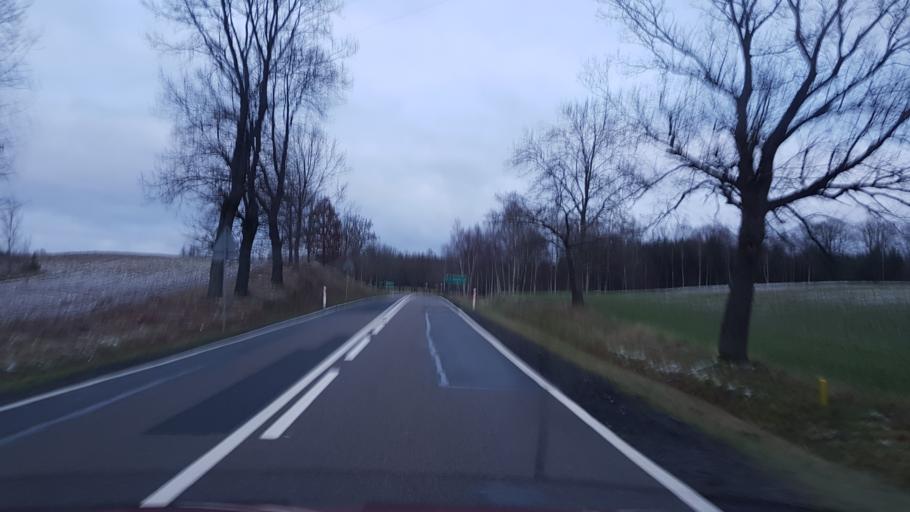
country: PL
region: Pomeranian Voivodeship
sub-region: Powiat bytowski
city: Tuchomie
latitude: 54.0712
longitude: 17.2827
